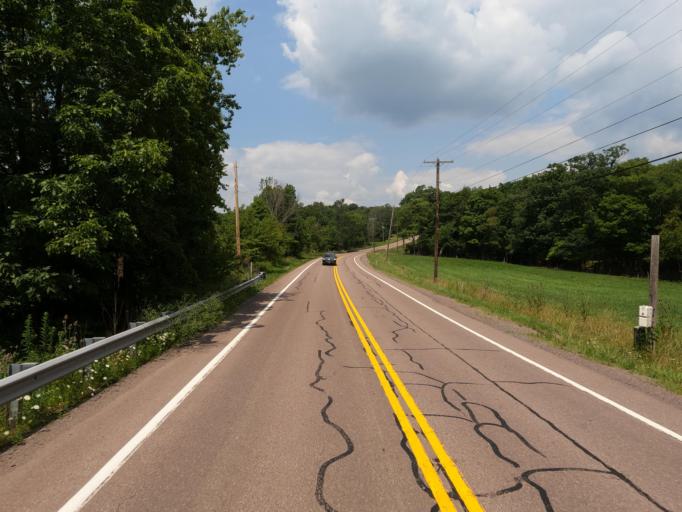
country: US
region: Maryland
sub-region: Allegany County
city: Westernport
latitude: 39.6280
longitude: -79.2150
